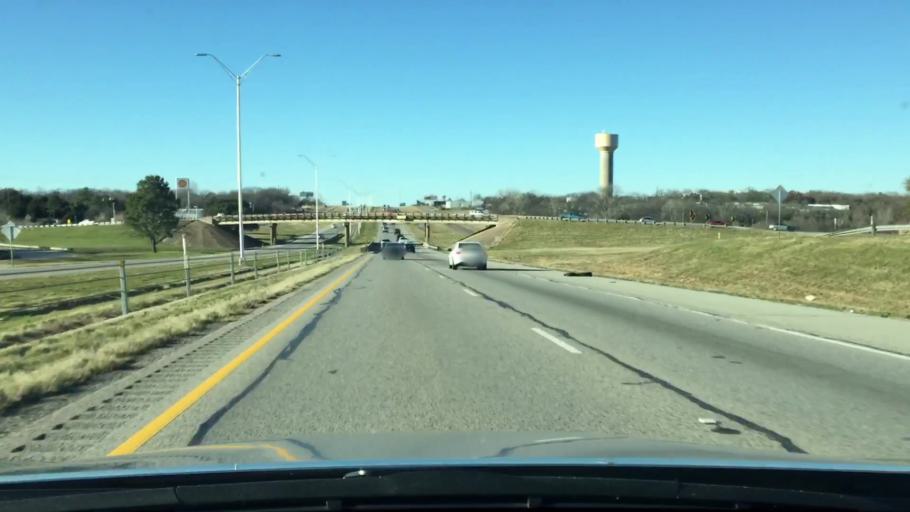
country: US
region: Texas
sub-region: Johnson County
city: Alvarado
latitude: 32.4632
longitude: -97.2653
